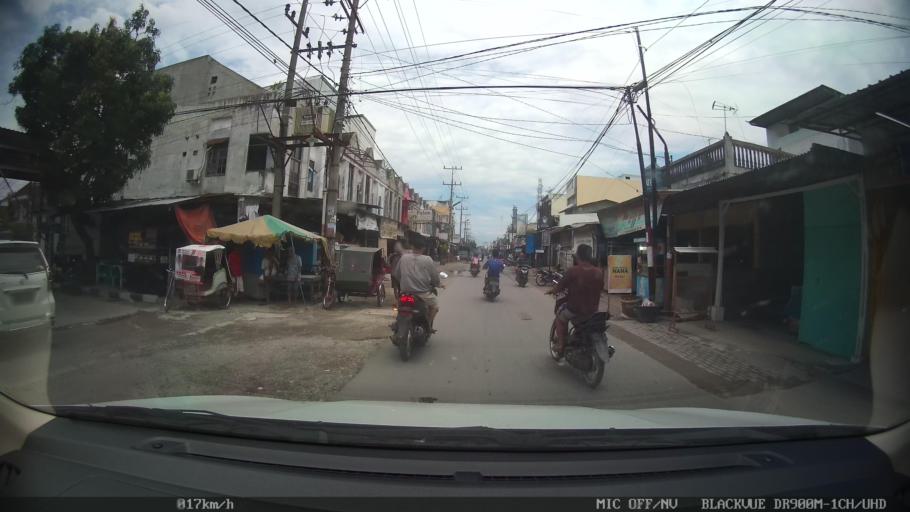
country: ID
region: North Sumatra
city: Sunggal
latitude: 3.6033
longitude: 98.5799
